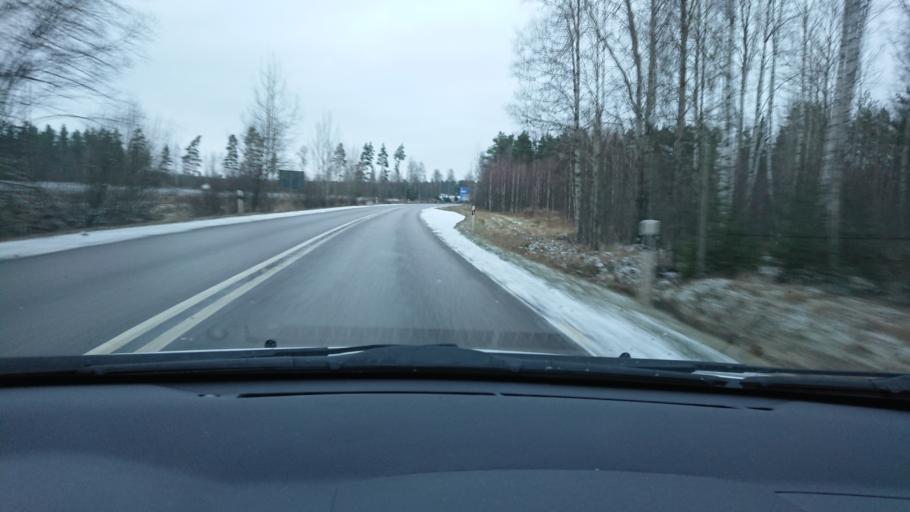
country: SE
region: Kalmar
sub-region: Hultsfreds Kommun
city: Hultsfred
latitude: 57.4967
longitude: 15.8209
